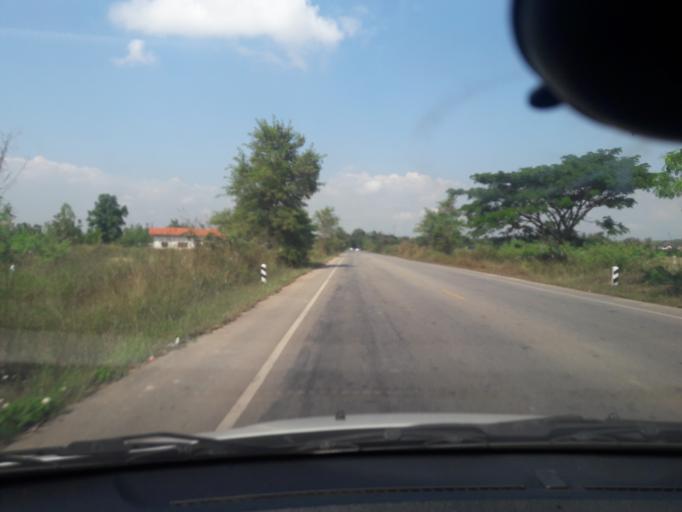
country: TH
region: Lampang
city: Mae Tha
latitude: 18.2065
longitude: 99.4991
